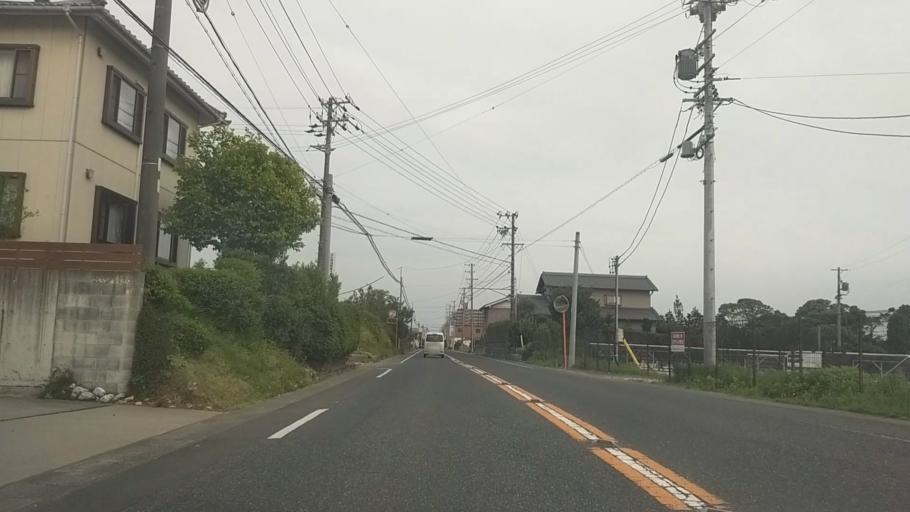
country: JP
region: Shizuoka
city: Hamamatsu
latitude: 34.7447
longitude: 137.6739
